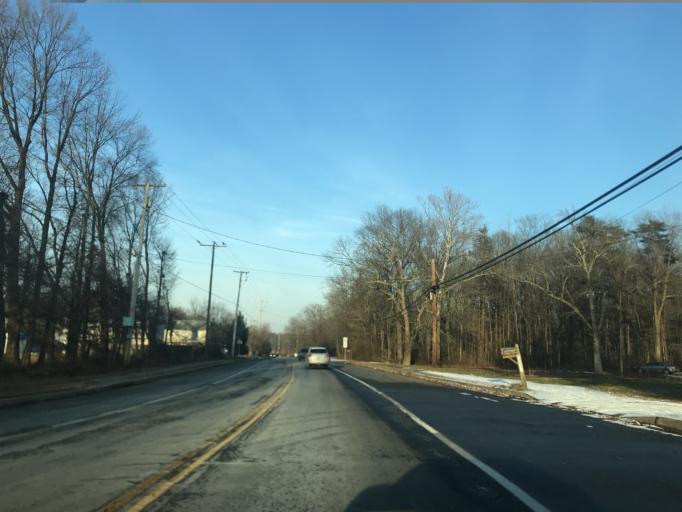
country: US
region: Maryland
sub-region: Harford County
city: Edgewood
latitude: 39.4254
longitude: -76.2863
